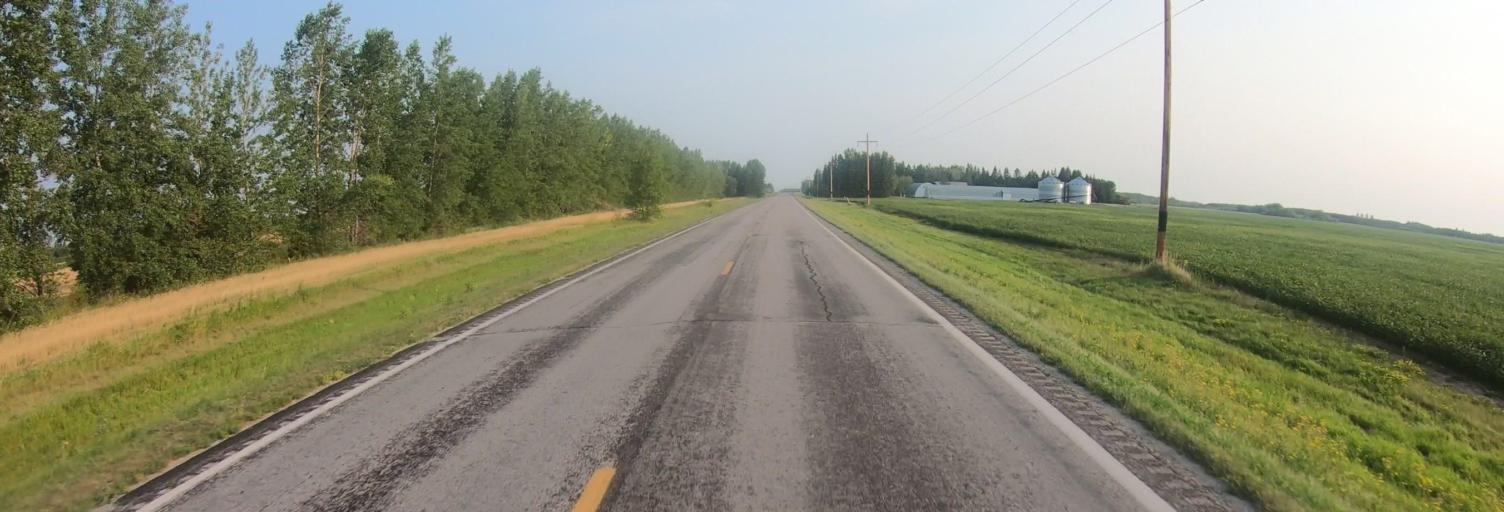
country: US
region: Minnesota
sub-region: Roseau County
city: Warroad
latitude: 48.7931
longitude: -95.3308
